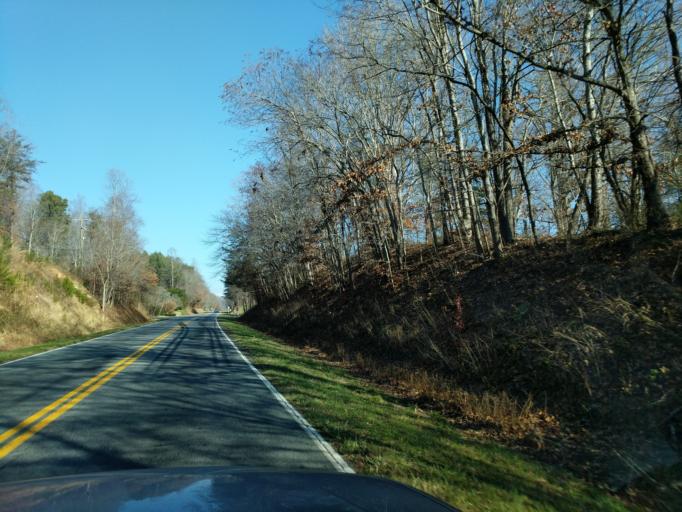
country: US
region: North Carolina
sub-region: McDowell County
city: West Marion
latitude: 35.6238
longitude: -81.9863
